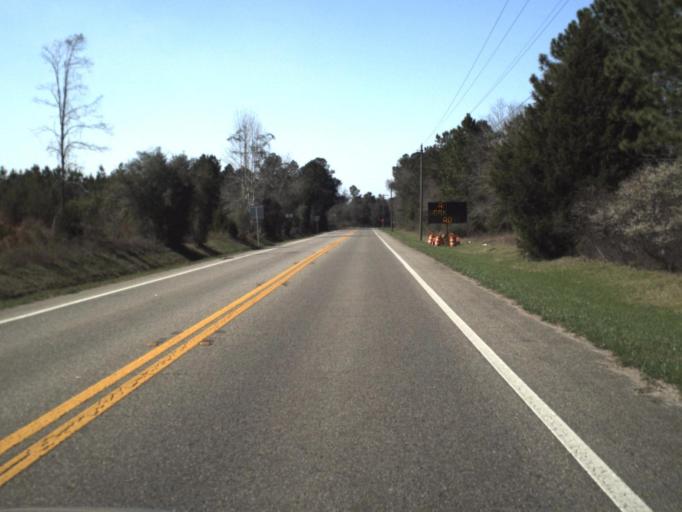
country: US
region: Florida
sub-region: Jackson County
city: Marianna
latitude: 30.6058
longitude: -85.1438
